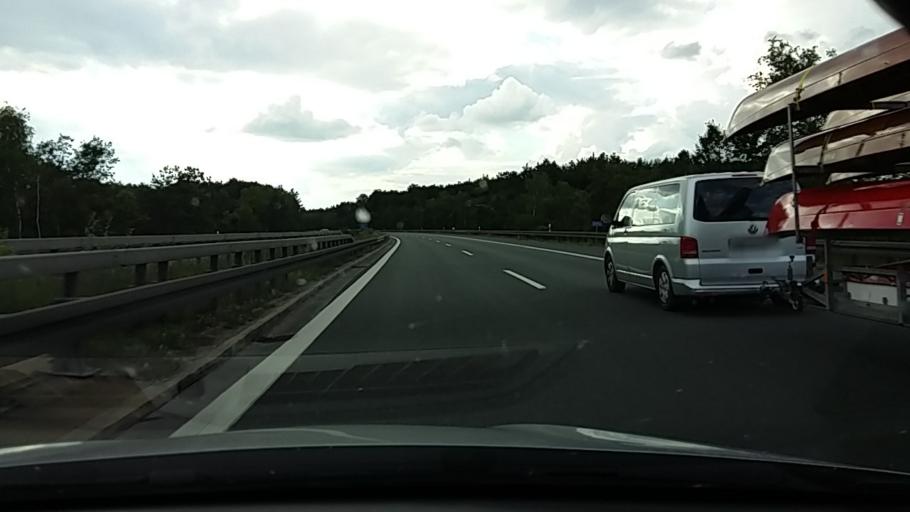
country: DE
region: Bavaria
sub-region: Upper Palatinate
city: Ursensollen
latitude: 49.4035
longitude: 11.7843
